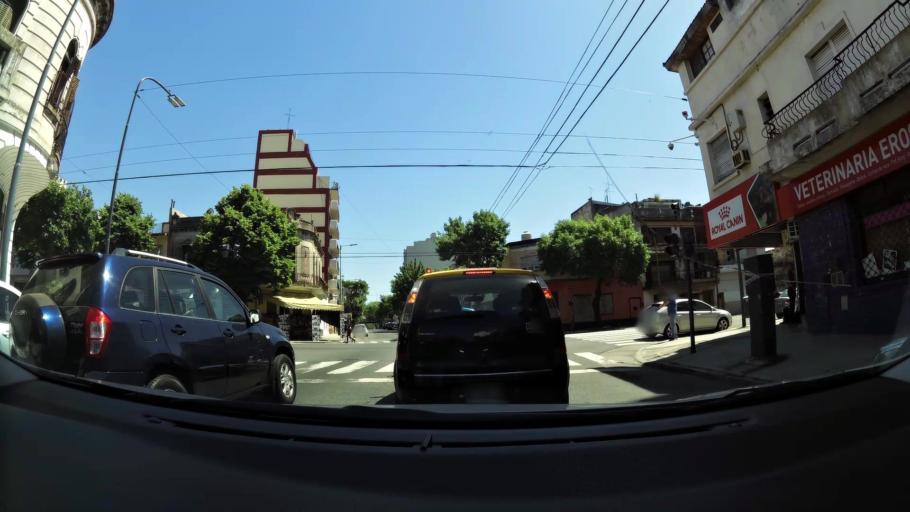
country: AR
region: Buenos Aires F.D.
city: Buenos Aires
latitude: -34.6307
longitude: -58.4191
